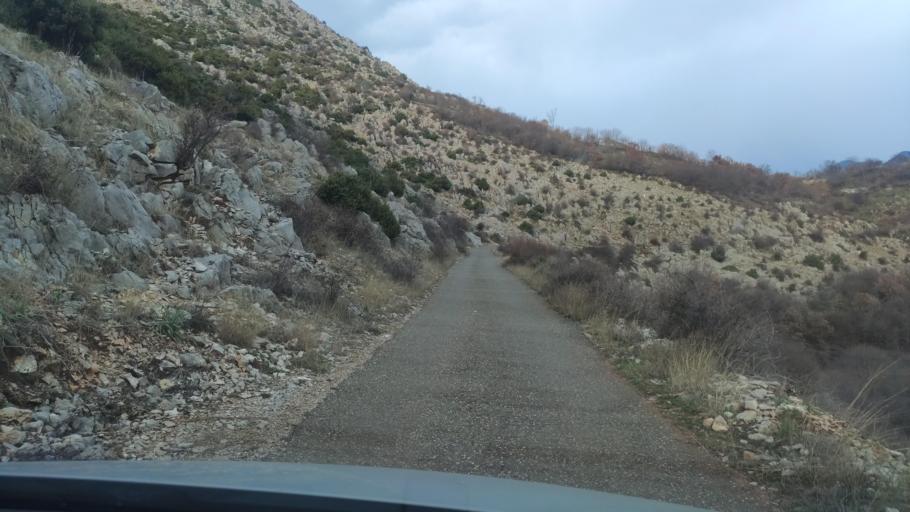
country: AL
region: Shkoder
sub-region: Rrethi i Malesia e Madhe
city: Gruemire
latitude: 42.2403
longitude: 19.5347
